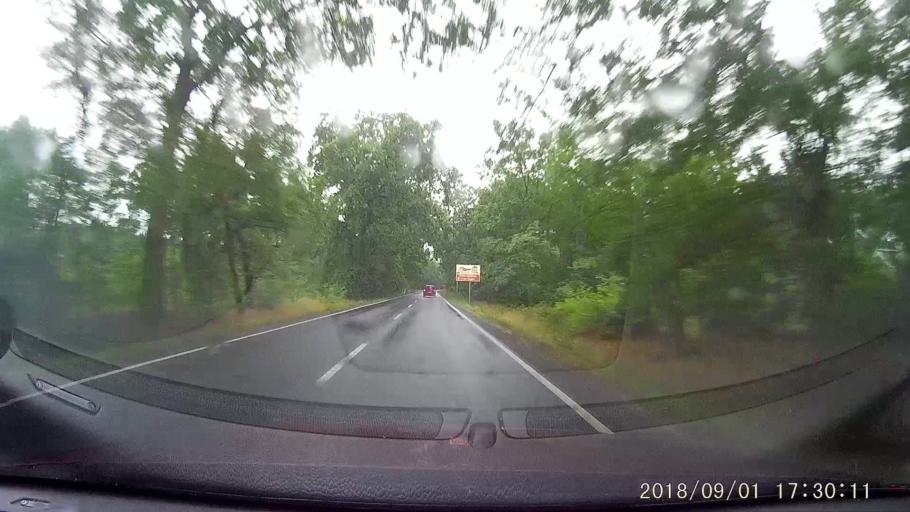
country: PL
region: Lubusz
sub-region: Powiat zaganski
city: Zagan
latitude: 51.6444
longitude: 15.3182
